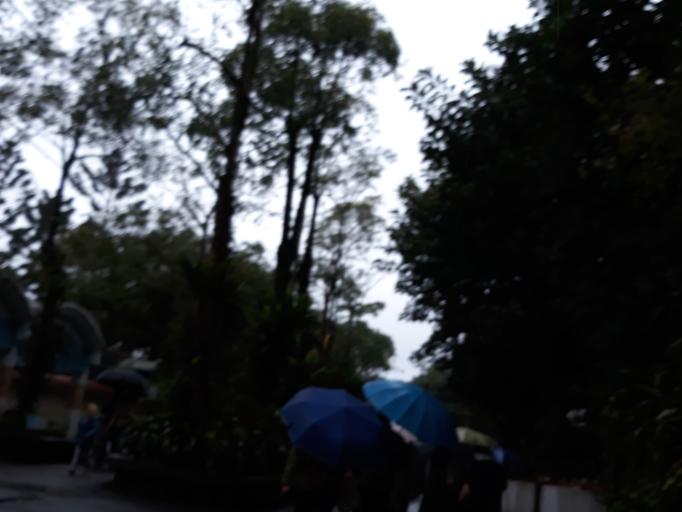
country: TW
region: Taipei
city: Taipei
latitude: 24.9977
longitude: 121.5826
